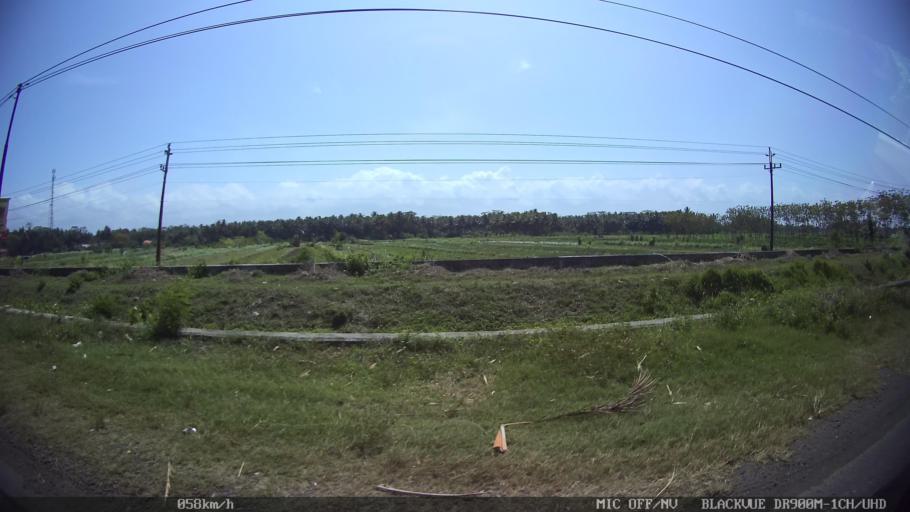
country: ID
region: Daerah Istimewa Yogyakarta
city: Srandakan
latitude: -7.9288
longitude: 110.1356
